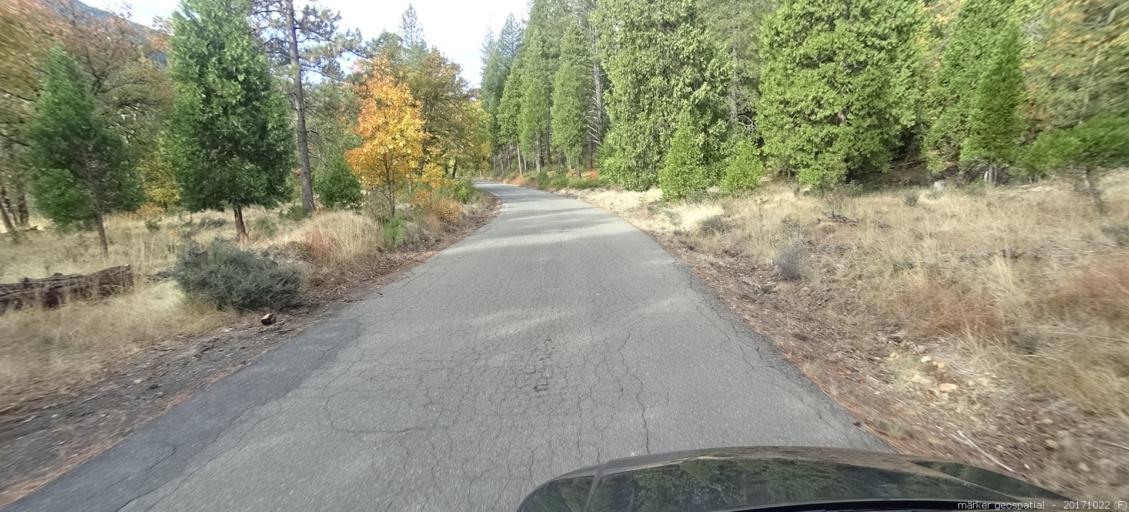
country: US
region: California
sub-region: Siskiyou County
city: Dunsmuir
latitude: 41.1556
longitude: -122.3528
